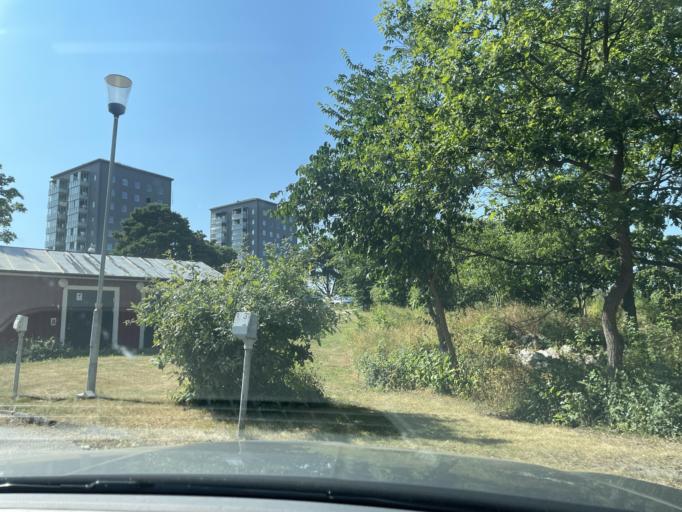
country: SE
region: Stockholm
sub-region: Stockholms Kommun
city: Arsta
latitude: 59.3091
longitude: 18.0149
